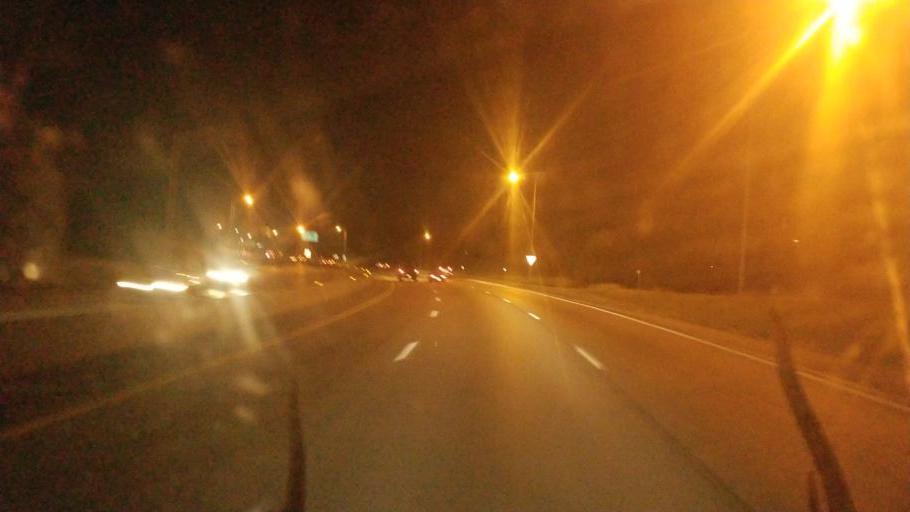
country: US
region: Missouri
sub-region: Jackson County
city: Kansas City
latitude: 39.0834
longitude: -94.5414
